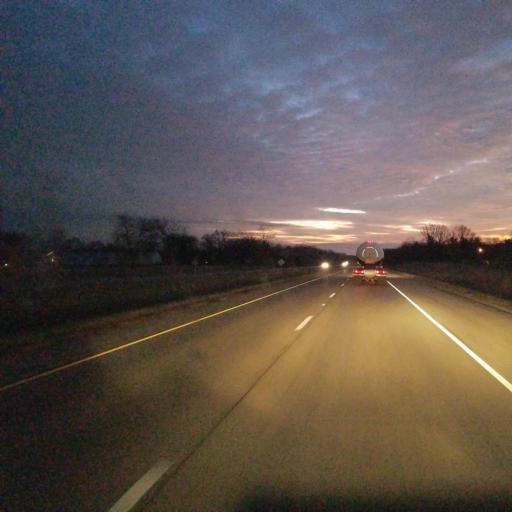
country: US
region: Illinois
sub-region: Peoria County
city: Bellevue
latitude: 40.6939
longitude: -89.6927
